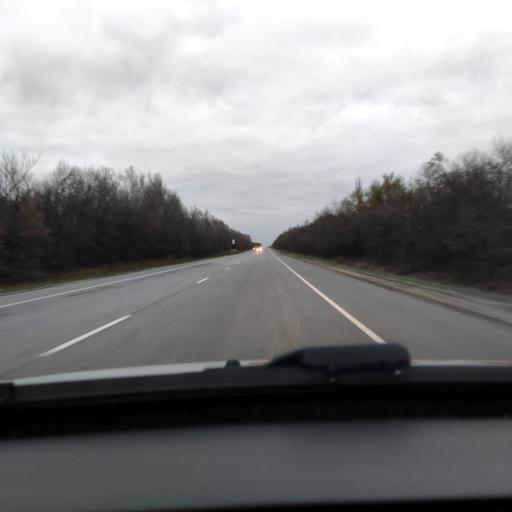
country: RU
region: Lipetsk
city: Khlevnoye
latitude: 52.3411
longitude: 39.1847
